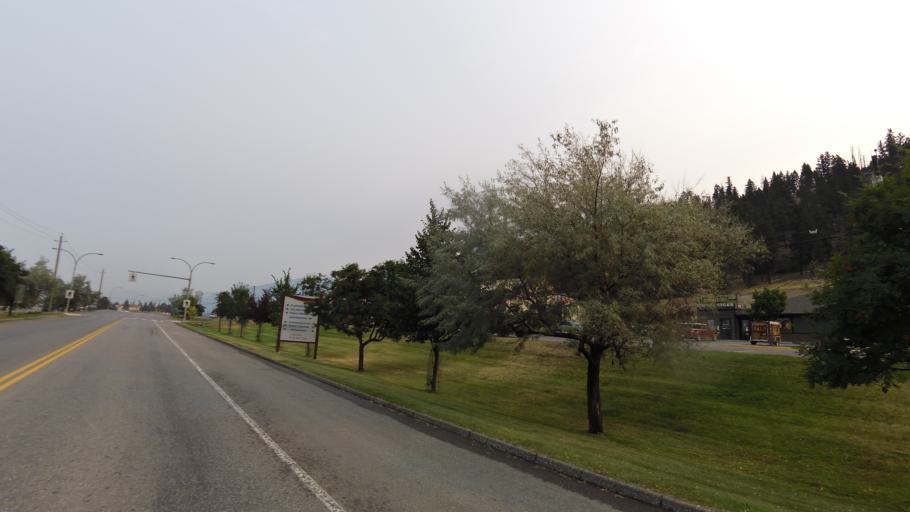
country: CA
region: British Columbia
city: Invermere
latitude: 50.6199
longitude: -116.0704
